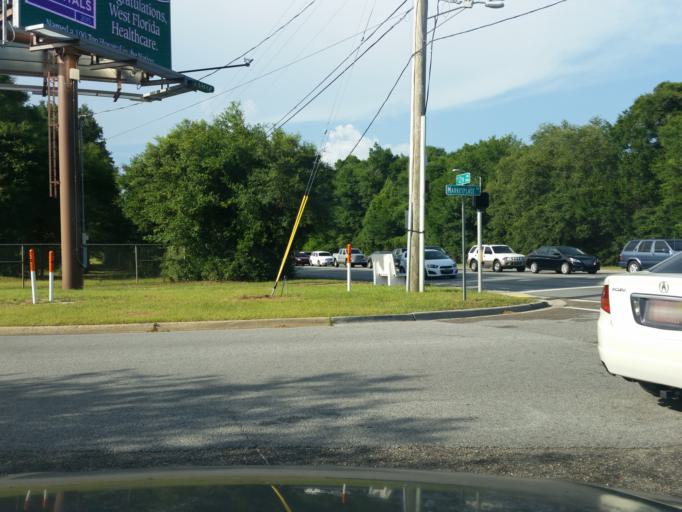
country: US
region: Florida
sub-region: Escambia County
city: Goulding
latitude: 30.4686
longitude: -87.2024
